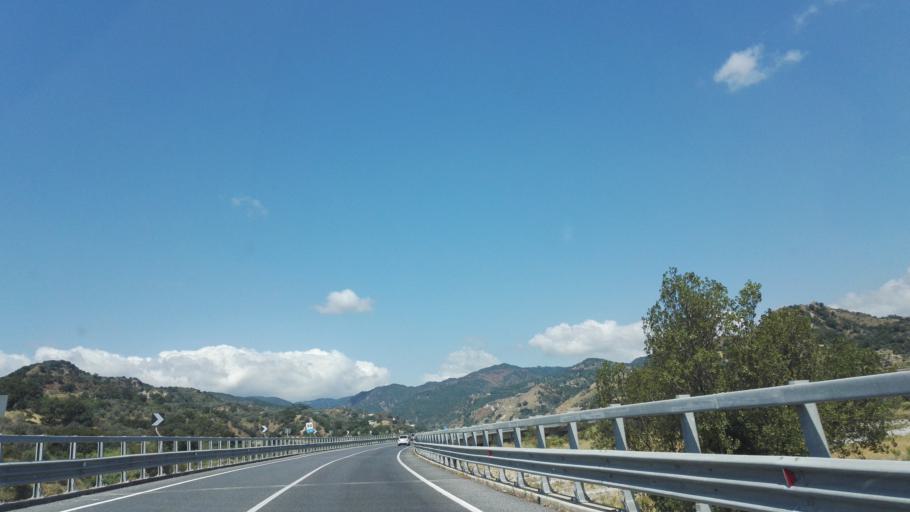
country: IT
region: Calabria
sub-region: Provincia di Reggio Calabria
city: Grotteria
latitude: 38.3442
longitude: 16.2611
